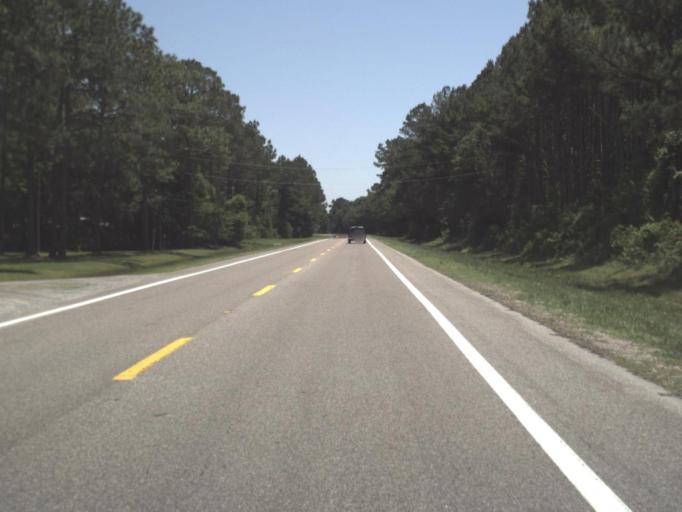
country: US
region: Florida
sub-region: Suwannee County
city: Wellborn
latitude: 30.2109
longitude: -82.8117
